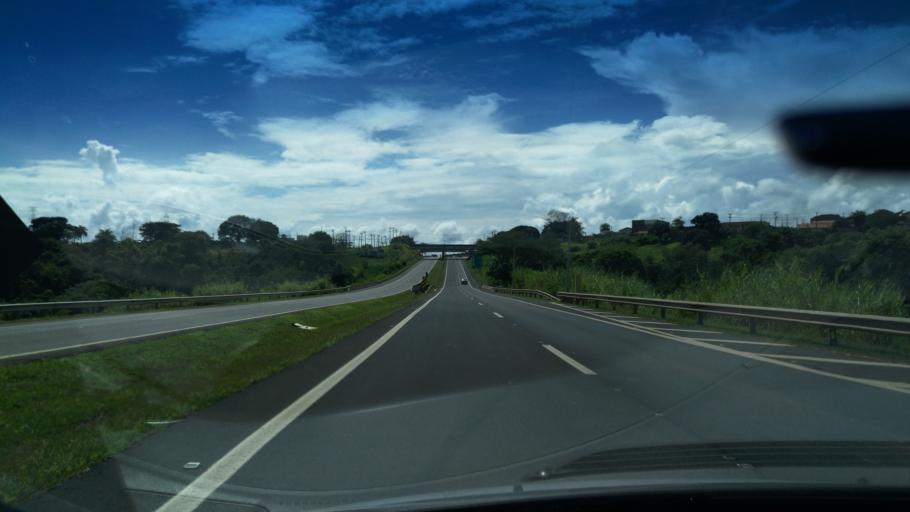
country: BR
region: Sao Paulo
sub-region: Santo Antonio Do Jardim
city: Espirito Santo do Pinhal
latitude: -22.1964
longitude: -46.7750
